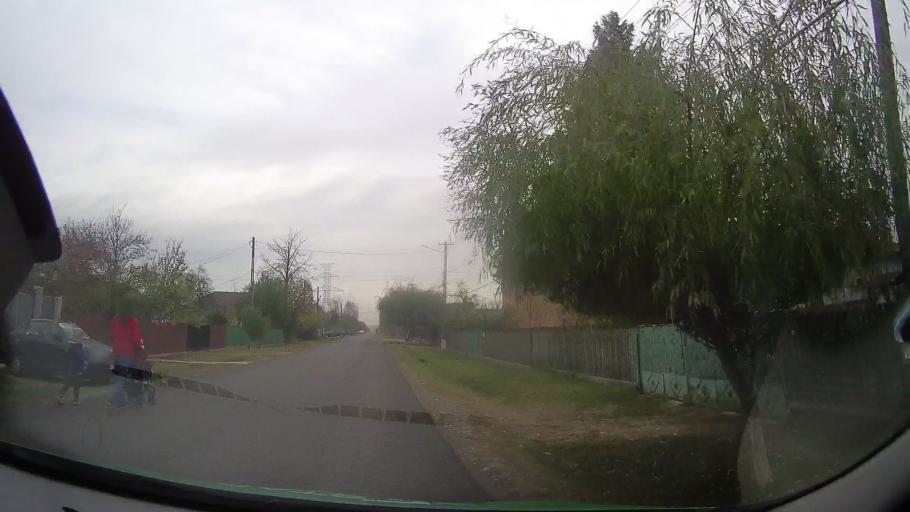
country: RO
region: Prahova
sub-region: Comuna Valea Calugareasca
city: Pantazi
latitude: 44.9311
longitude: 26.1435
